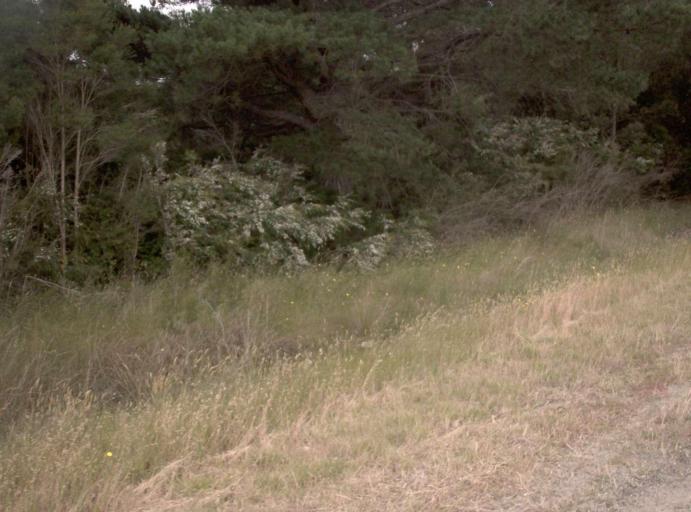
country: AU
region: Victoria
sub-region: Wellington
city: Sale
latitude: -38.1726
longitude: 147.0167
